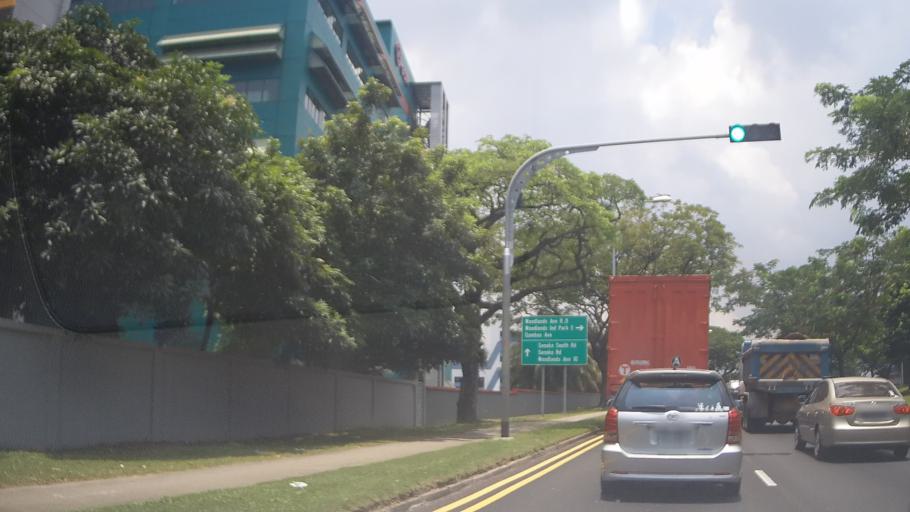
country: MY
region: Johor
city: Johor Bahru
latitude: 1.4562
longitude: 103.7985
